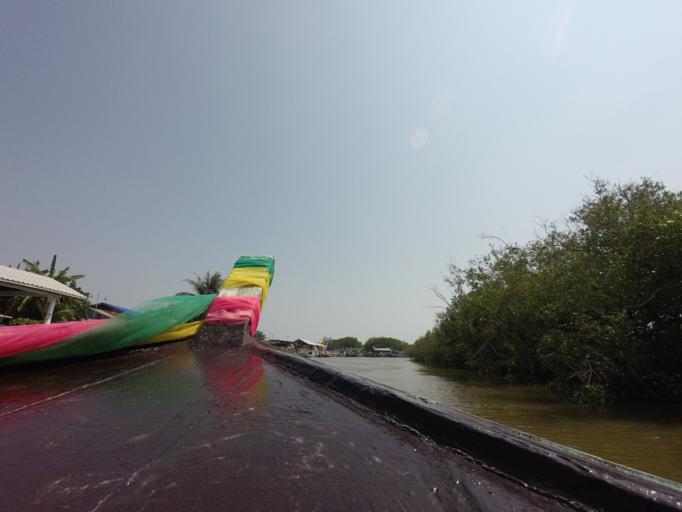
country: TH
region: Prachuap Khiri Khan
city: Kui Buri
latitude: 12.1364
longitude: 99.9664
